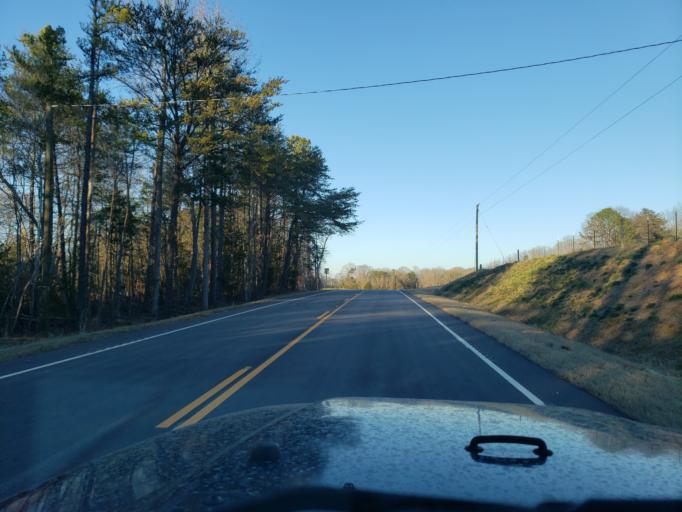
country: US
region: South Carolina
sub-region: Cherokee County
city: Blacksburg
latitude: 35.0235
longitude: -81.4035
